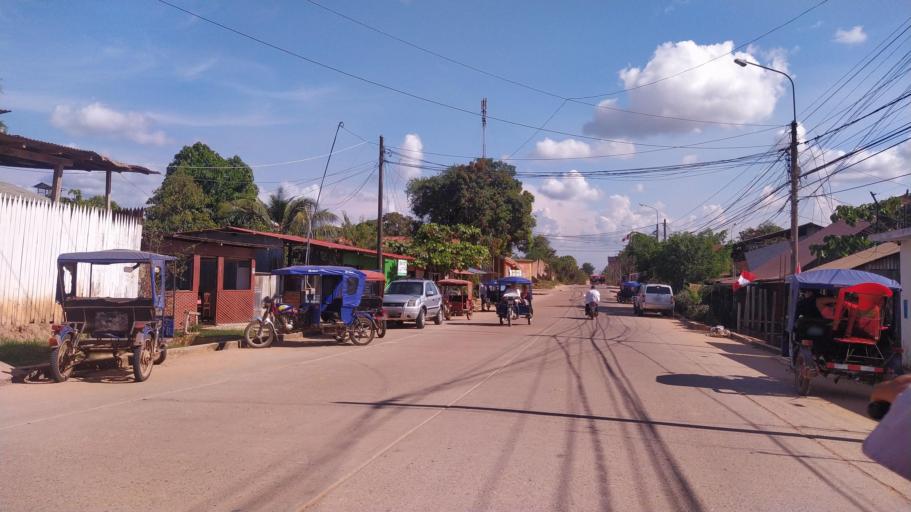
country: PE
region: Ucayali
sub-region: Provincia de Coronel Portillo
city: Puerto Callao
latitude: -8.3546
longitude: -74.5789
